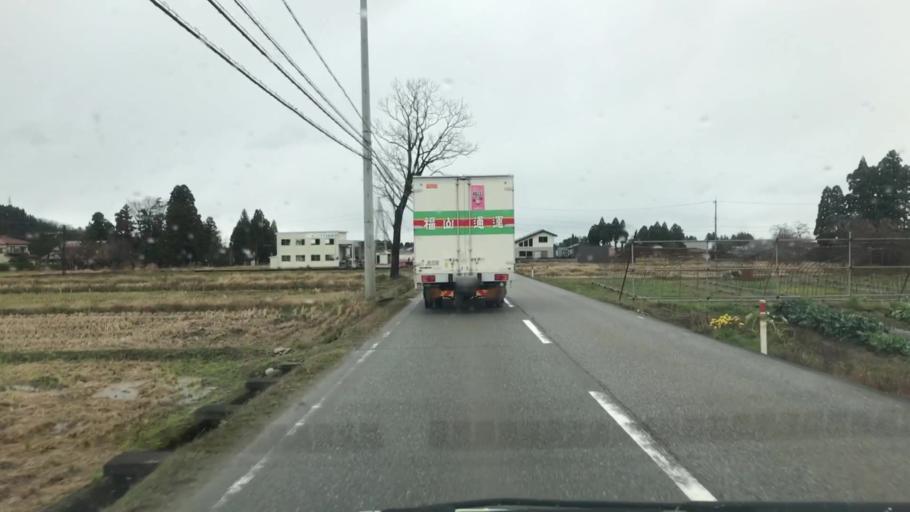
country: JP
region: Toyama
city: Kamiichi
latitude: 36.5967
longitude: 137.3251
